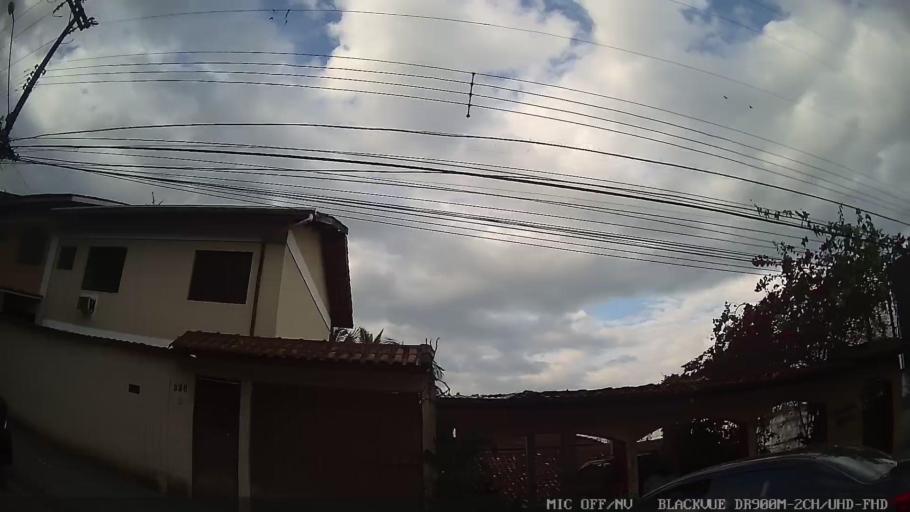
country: BR
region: Sao Paulo
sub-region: Guaruja
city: Guaruja
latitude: -23.9800
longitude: -46.2384
